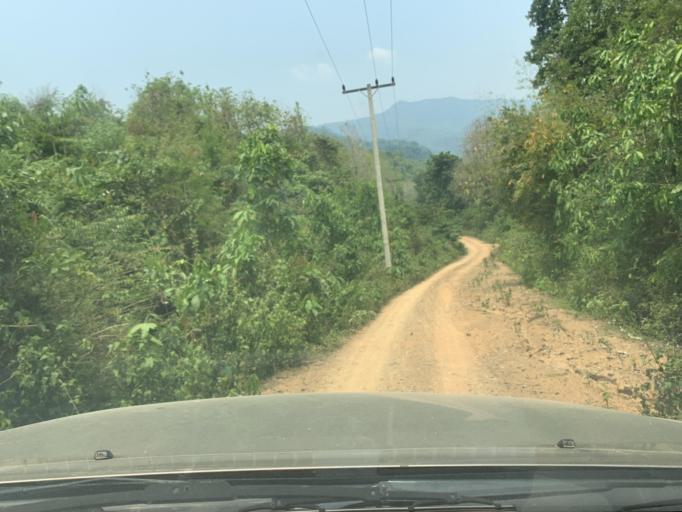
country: LA
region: Louangphabang
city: Louangphabang
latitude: 19.9608
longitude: 102.1280
